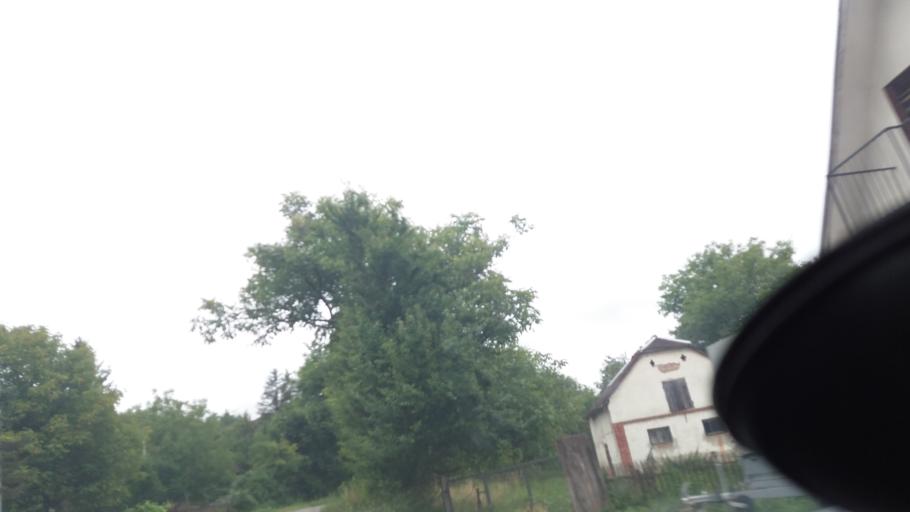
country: RS
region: Central Serbia
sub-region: Kolubarski Okrug
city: Ljig
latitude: 44.2227
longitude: 20.1699
